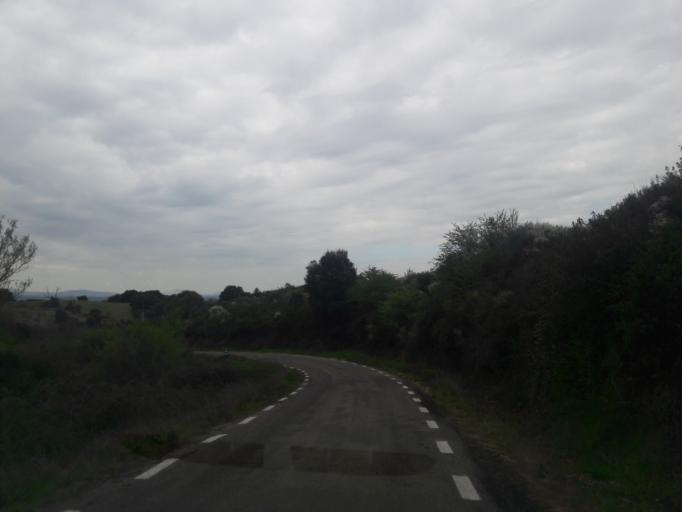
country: ES
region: Castille and Leon
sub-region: Provincia de Salamanca
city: Serradilla del Arroyo
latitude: 40.5100
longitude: -6.3981
